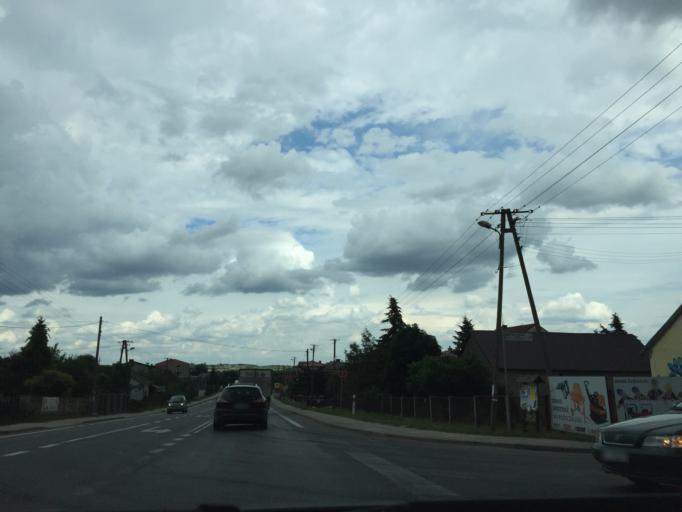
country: PL
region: Swietokrzyskie
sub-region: Powiat kielecki
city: Checiny
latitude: 50.7655
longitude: 20.4446
